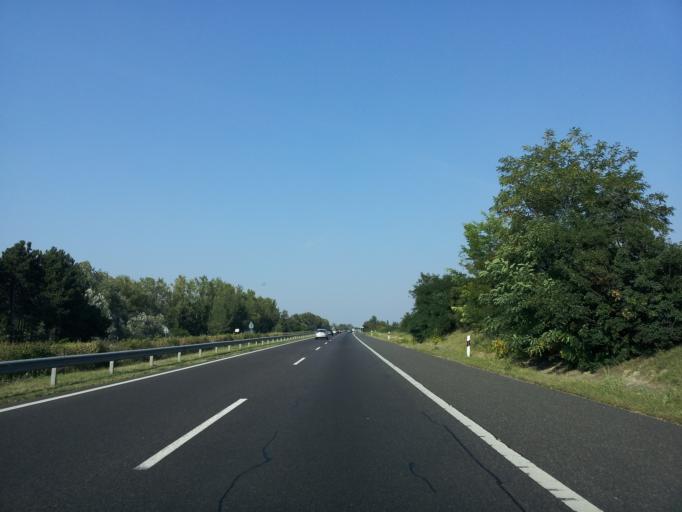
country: HU
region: Fejer
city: Szabadbattyan
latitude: 47.1218
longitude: 18.3990
